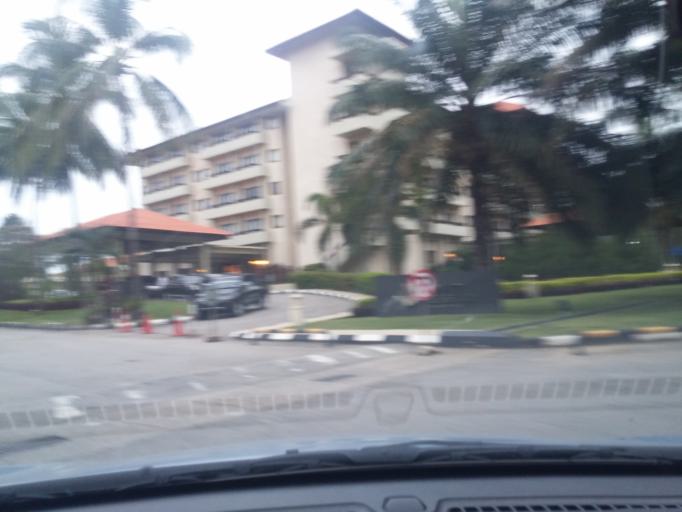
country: MY
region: Pahang
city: Kuantan
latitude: 3.8115
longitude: 103.3710
